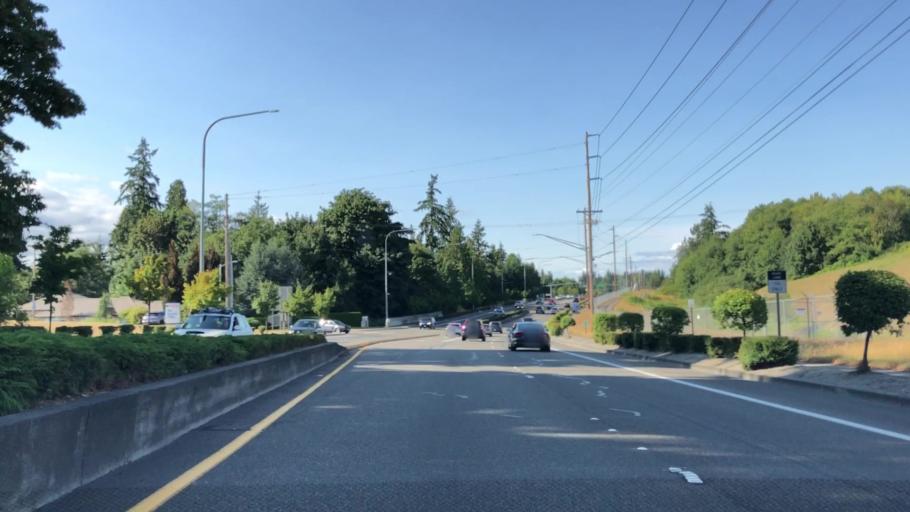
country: US
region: Washington
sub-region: Snohomish County
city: Mukilteo
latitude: 47.9015
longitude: -122.2927
